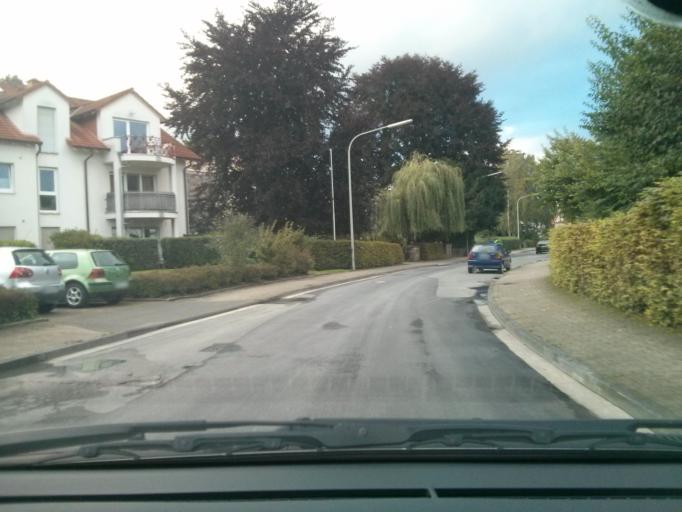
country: DE
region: North Rhine-Westphalia
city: Wickede
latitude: 51.4457
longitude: 7.9599
